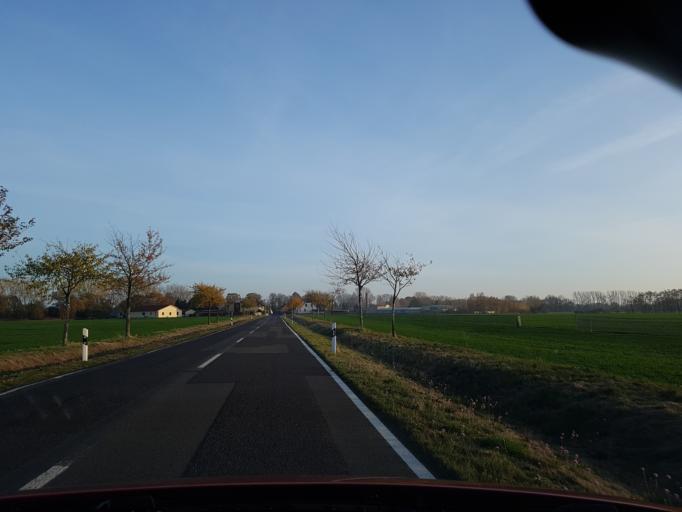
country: DE
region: Saxony
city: Nauwalde
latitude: 51.4435
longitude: 13.4425
